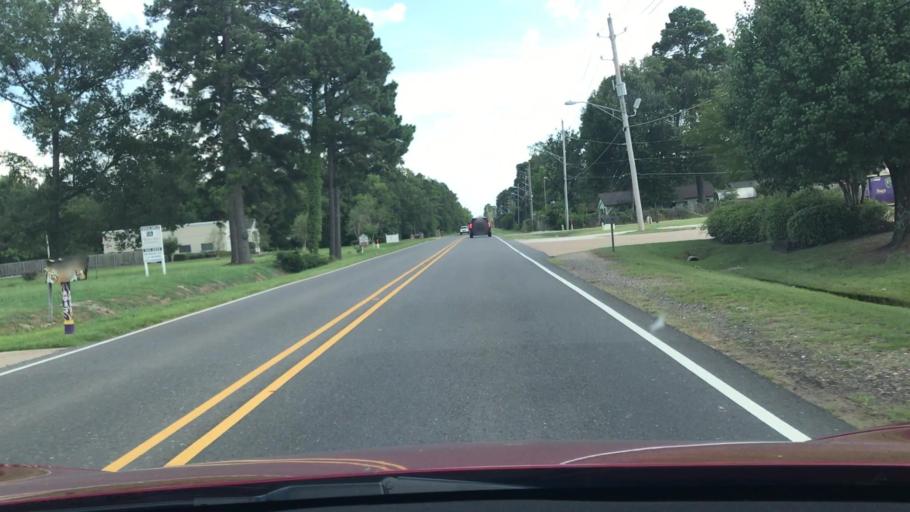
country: US
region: Louisiana
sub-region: Bossier Parish
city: Bossier City
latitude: 32.3974
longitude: -93.7386
